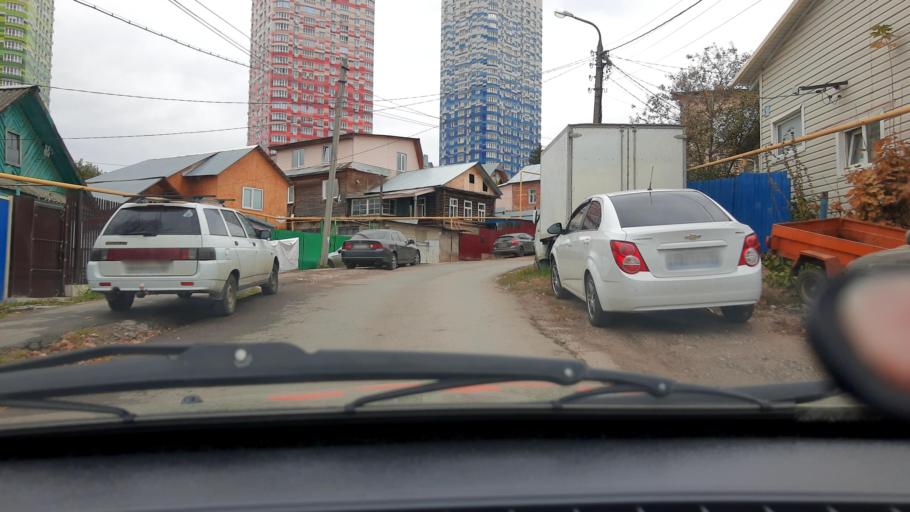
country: RU
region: Bashkortostan
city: Ufa
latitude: 54.7735
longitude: 56.0425
